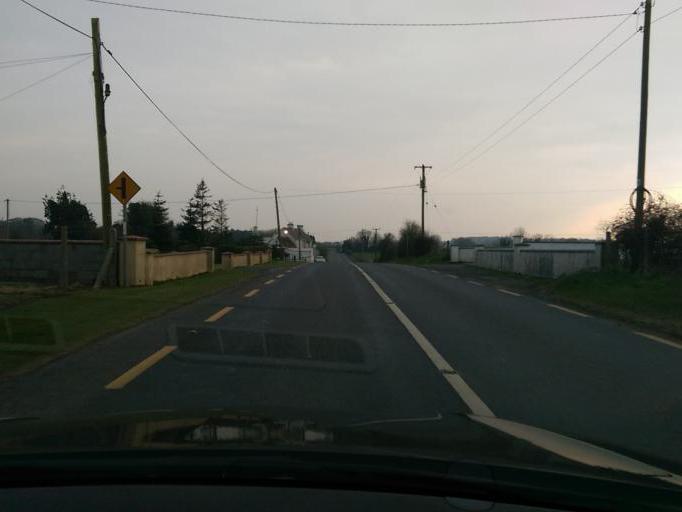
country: IE
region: Leinster
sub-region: An Longfort
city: Ballymahon
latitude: 53.5149
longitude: -7.8223
